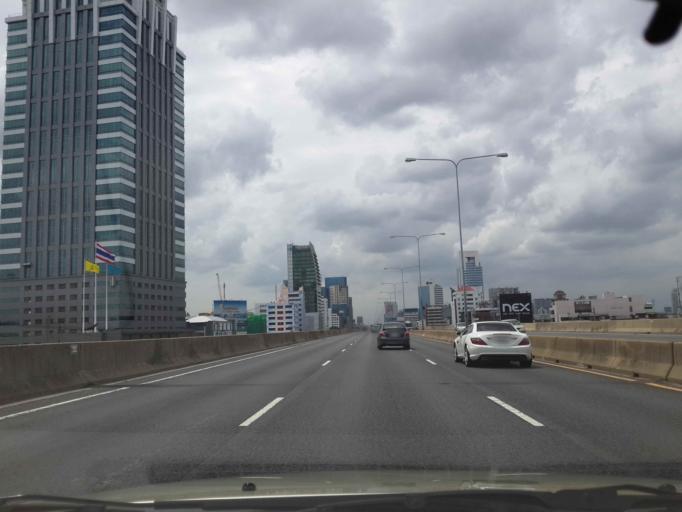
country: TH
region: Bangkok
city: Phaya Thai
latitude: 13.7941
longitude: 100.5612
